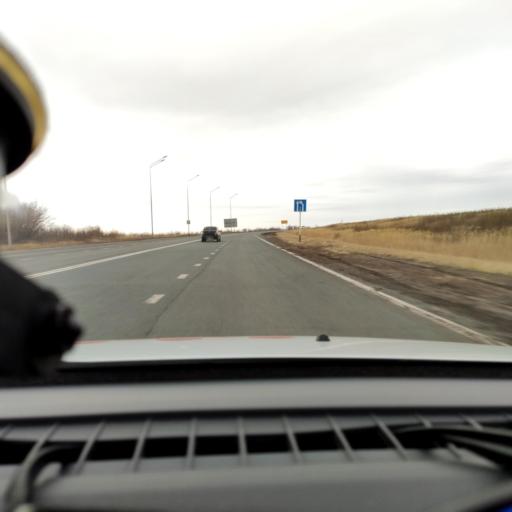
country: RU
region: Samara
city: Smyshlyayevka
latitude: 53.1439
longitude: 50.3899
